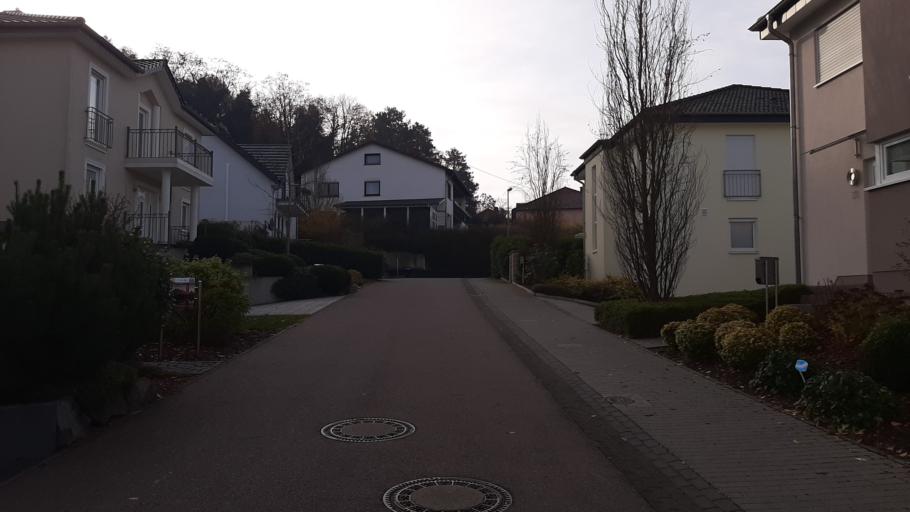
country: DE
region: Saarland
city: Perl
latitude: 49.4680
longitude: 6.3805
